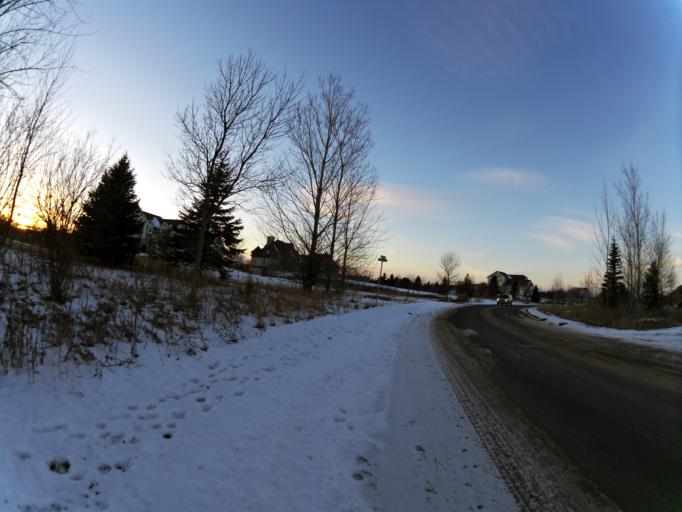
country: US
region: Minnesota
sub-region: Washington County
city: Lake Elmo
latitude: 44.9775
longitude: -92.8507
